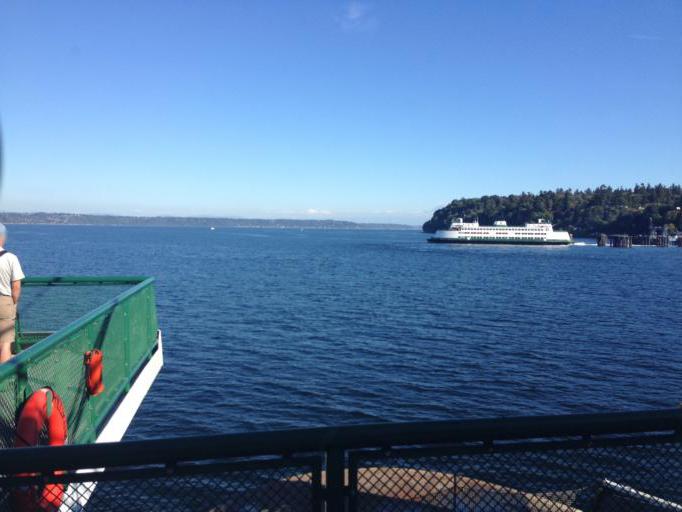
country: US
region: Washington
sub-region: Kitsap County
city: Southworth
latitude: 47.5152
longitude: -122.4655
